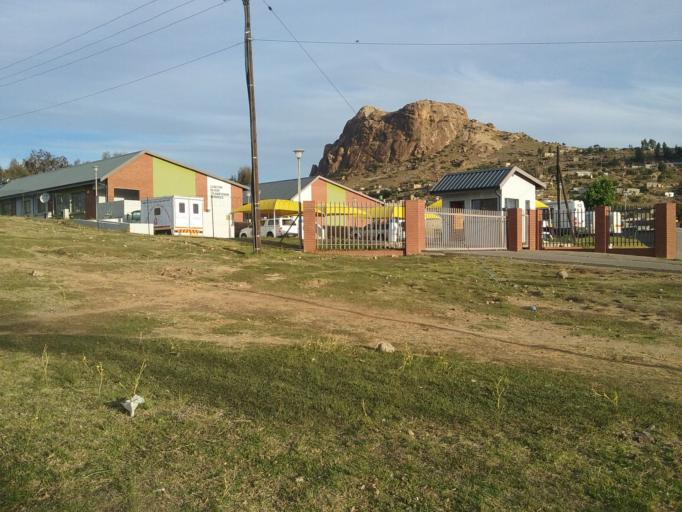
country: LS
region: Maseru
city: Maseru
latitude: -29.3467
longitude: 27.5254
